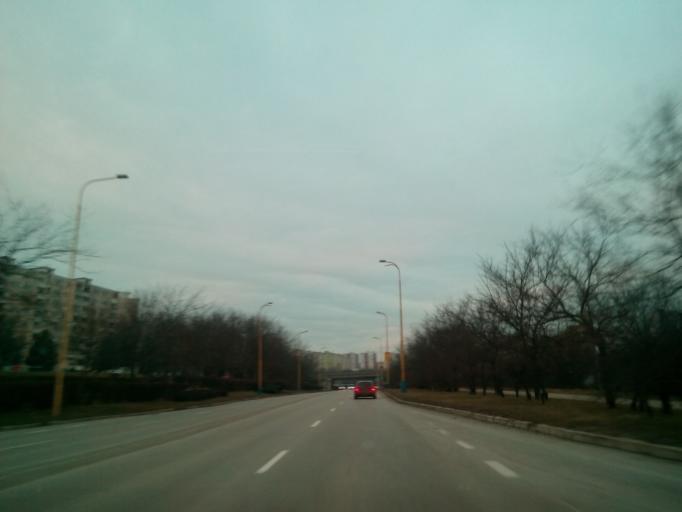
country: SK
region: Kosicky
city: Kosice
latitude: 48.7099
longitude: 21.2182
